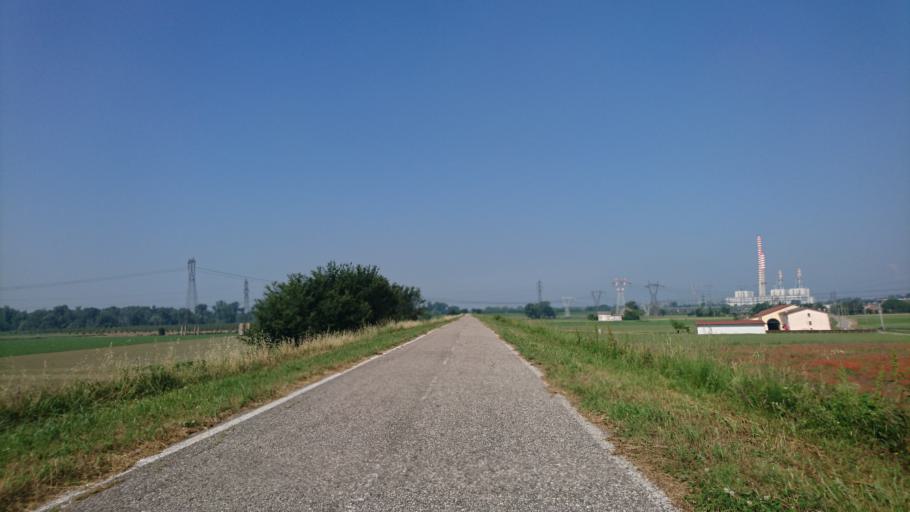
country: IT
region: Lombardy
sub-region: Provincia di Mantova
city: Ostiglia
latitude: 45.0567
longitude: 11.1582
